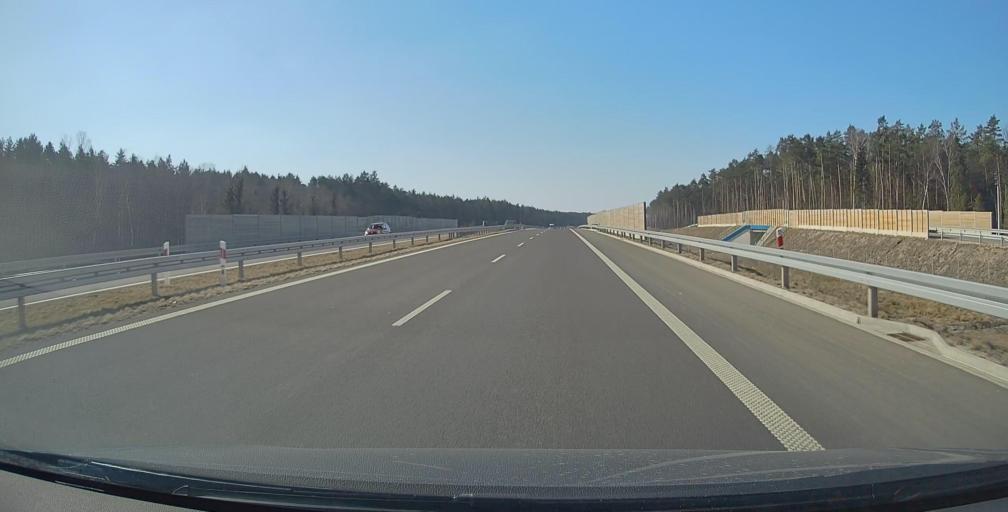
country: PL
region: Lublin Voivodeship
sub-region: Powiat janowski
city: Modliborzyce
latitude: 50.6618
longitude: 22.3156
